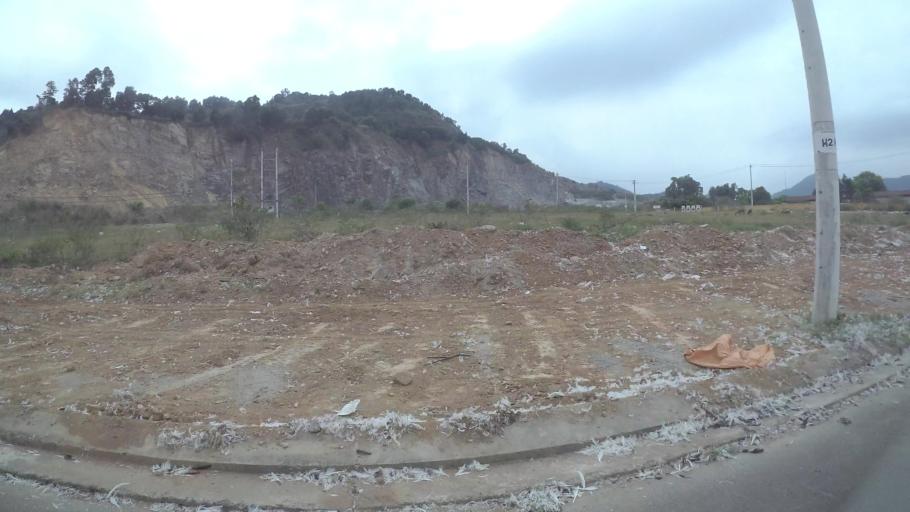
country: VN
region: Da Nang
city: Lien Chieu
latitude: 16.0421
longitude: 108.1668
